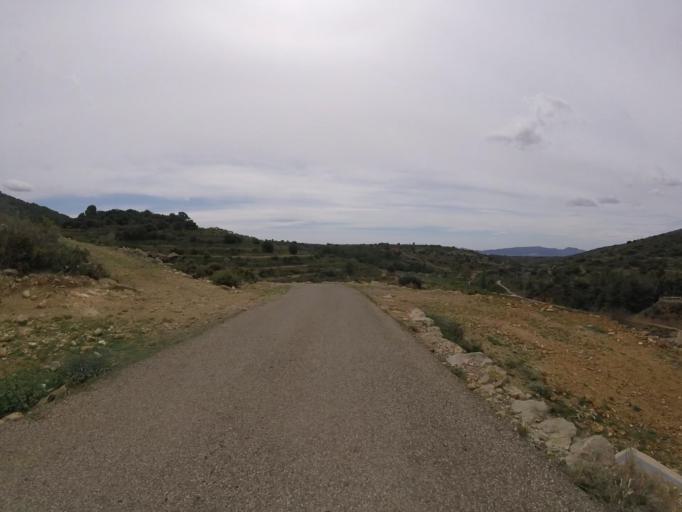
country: ES
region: Valencia
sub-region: Provincia de Castello
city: Sierra-Engarceran
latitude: 40.2633
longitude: -0.0227
